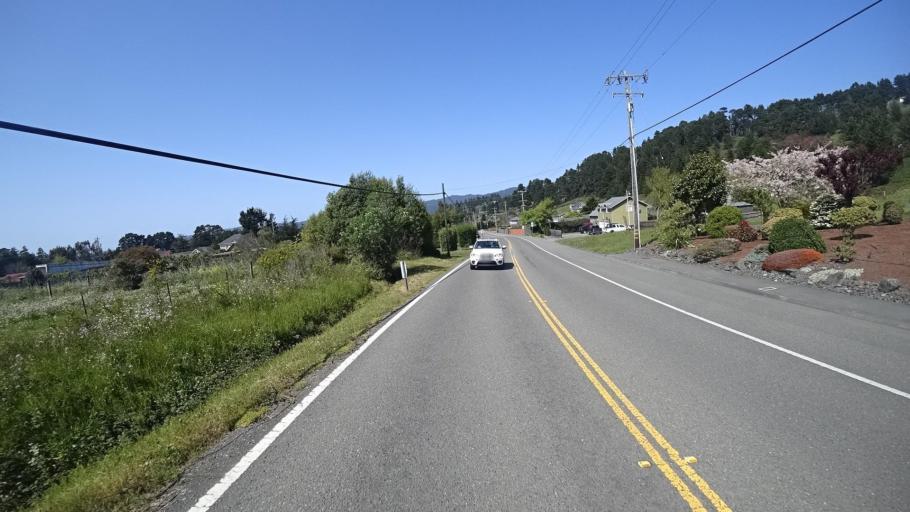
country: US
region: California
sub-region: Humboldt County
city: Hydesville
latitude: 40.5621
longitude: -124.1269
